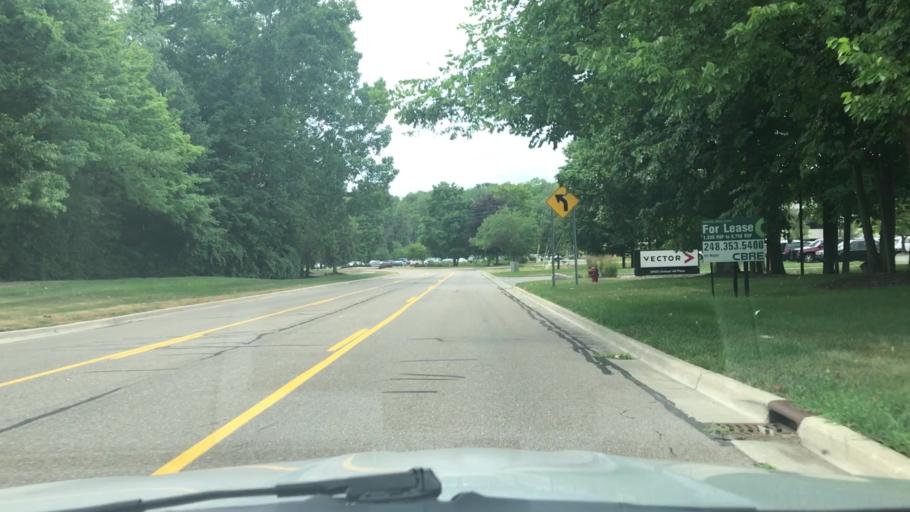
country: US
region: Michigan
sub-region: Wayne County
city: Northville
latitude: 42.4447
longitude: -83.4366
